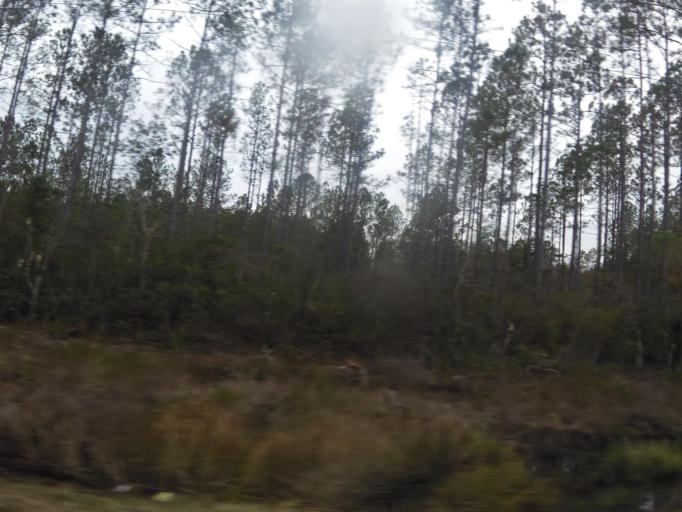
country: US
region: Georgia
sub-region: Charlton County
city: Folkston
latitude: 30.8687
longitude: -82.0417
